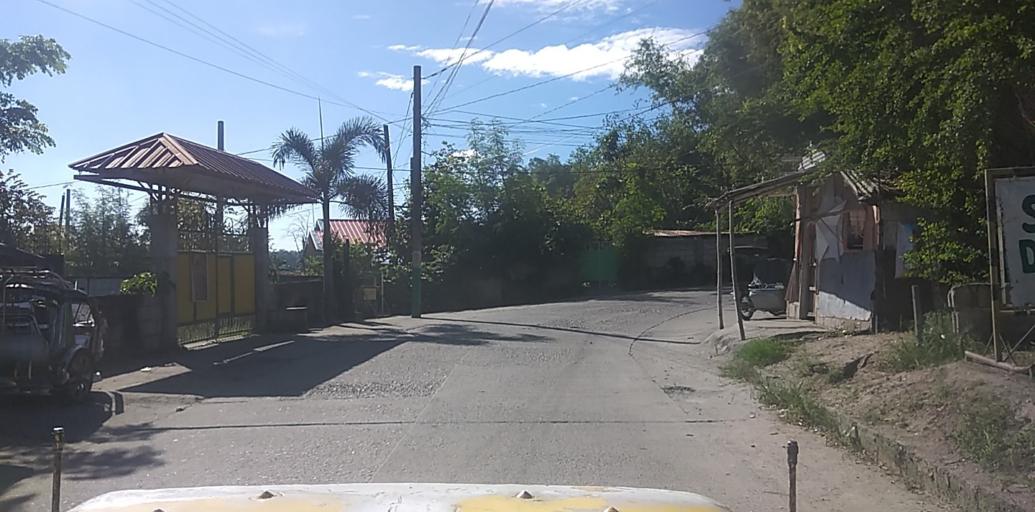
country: PH
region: Central Luzon
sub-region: Province of Pampanga
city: San Patricio
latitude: 15.0922
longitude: 120.7131
